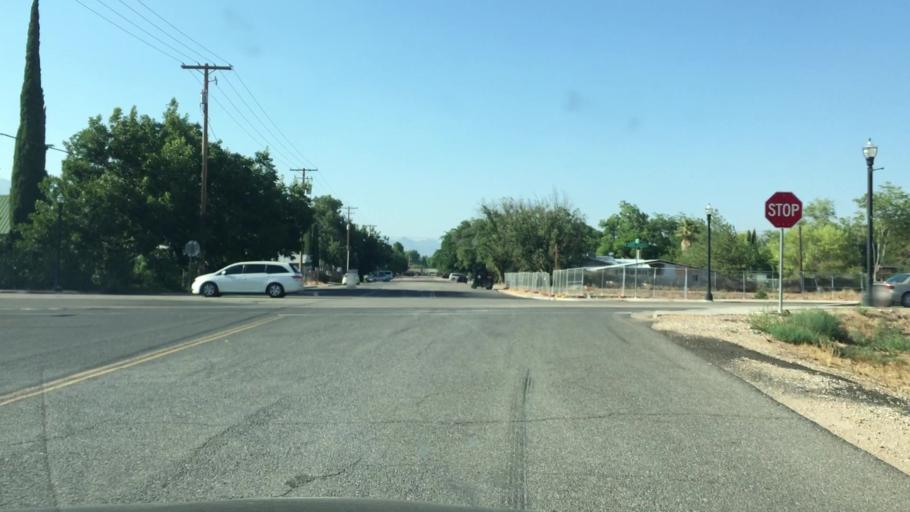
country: US
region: Utah
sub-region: Washington County
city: Hurricane
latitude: 37.1763
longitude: -113.2862
